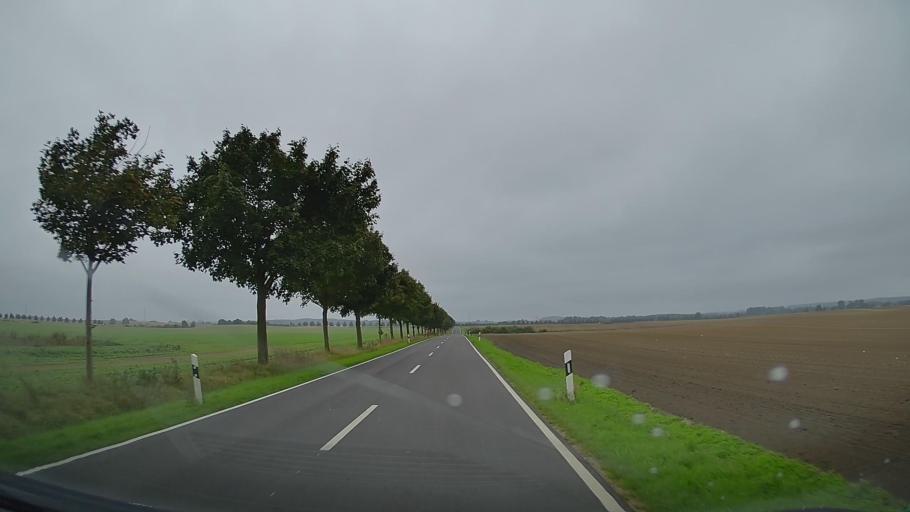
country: DE
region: Mecklenburg-Vorpommern
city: Tarnow
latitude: 53.7791
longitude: 12.0823
